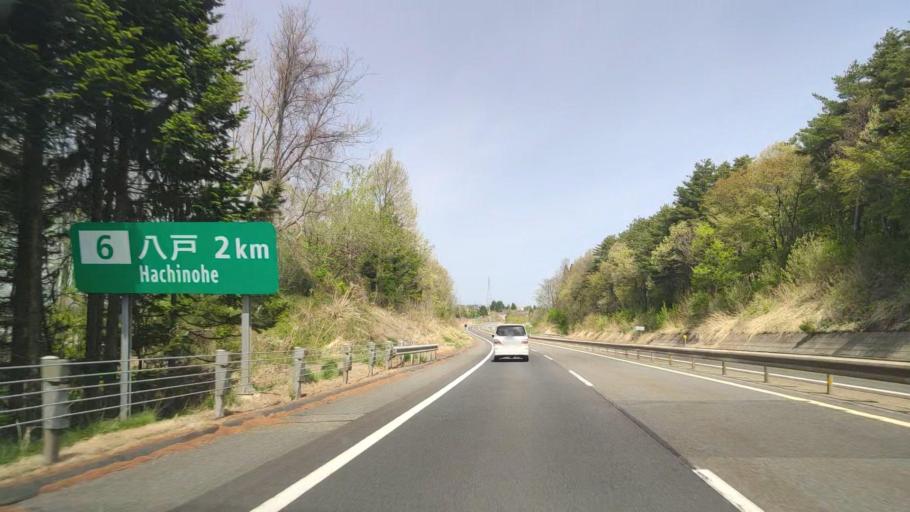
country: JP
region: Aomori
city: Hachinohe
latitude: 40.4718
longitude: 141.4613
